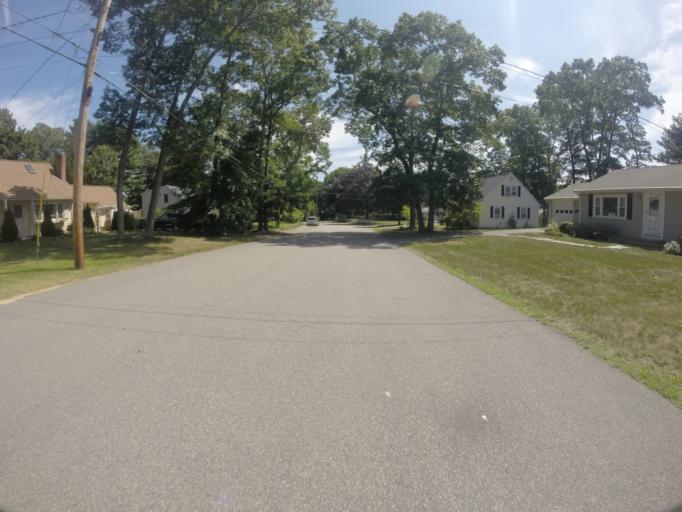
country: US
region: Massachusetts
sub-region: Bristol County
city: Easton
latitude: 42.0561
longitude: -71.1035
